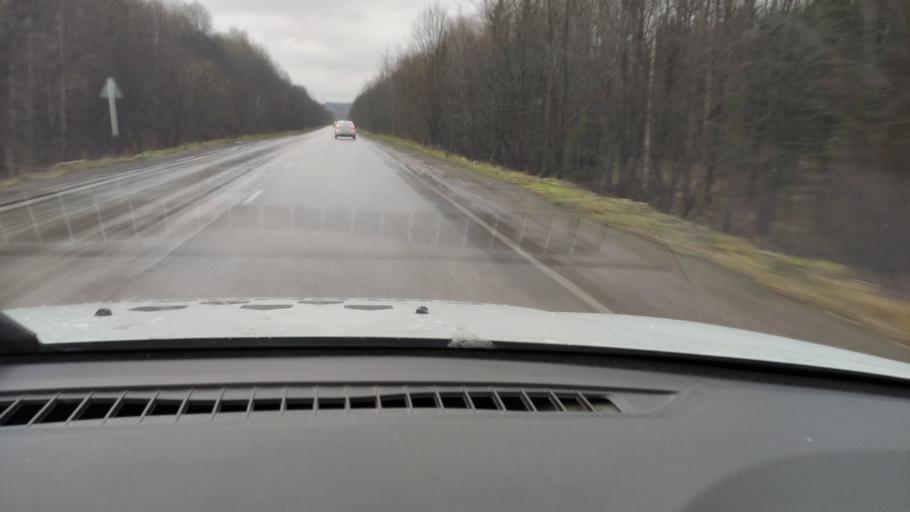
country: RU
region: Perm
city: Novyye Lyady
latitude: 58.0218
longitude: 56.6568
